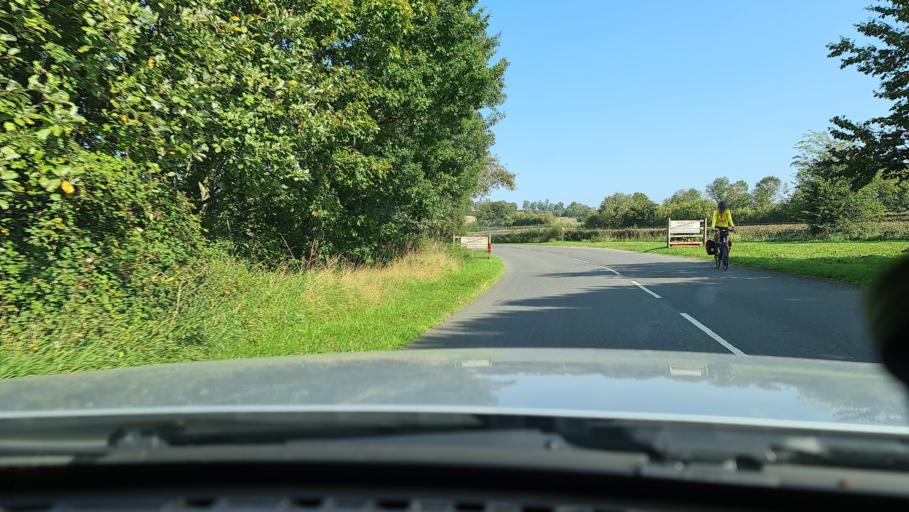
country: GB
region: England
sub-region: Northamptonshire
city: Brackley
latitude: 52.1412
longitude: -1.1594
